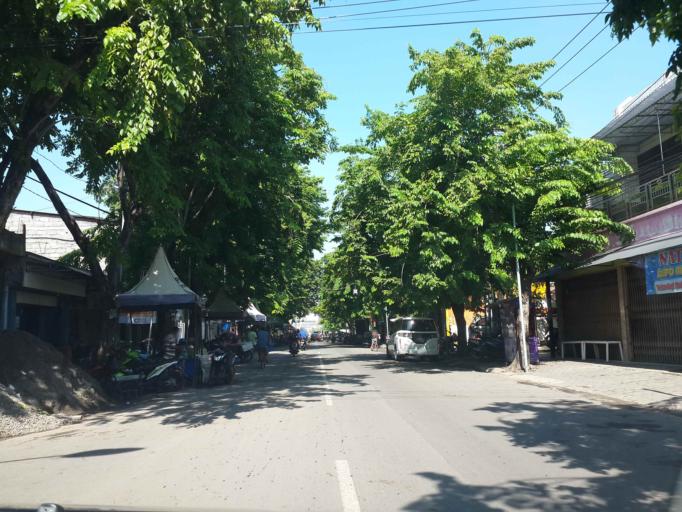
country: ID
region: East Java
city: Gresik
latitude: -7.1721
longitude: 112.6558
